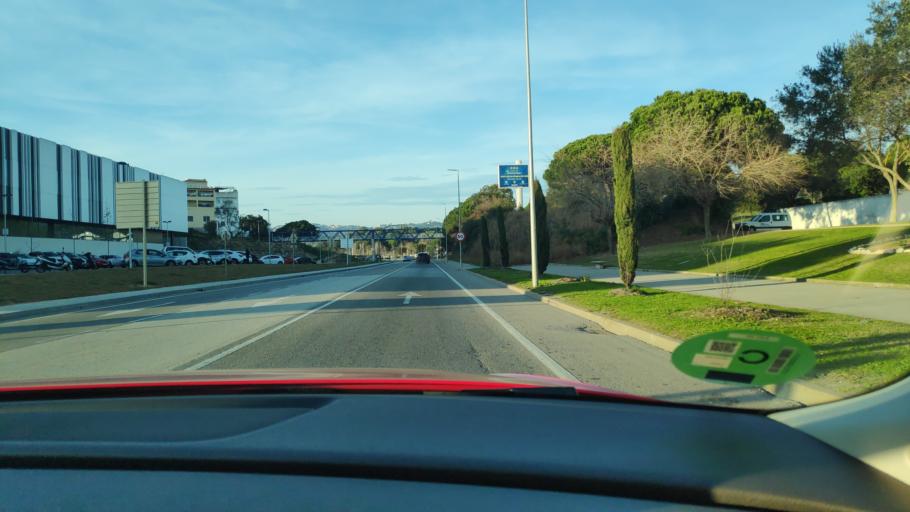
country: ES
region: Catalonia
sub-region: Provincia de Girona
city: Lloret de Mar
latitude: 41.7047
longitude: 2.8357
